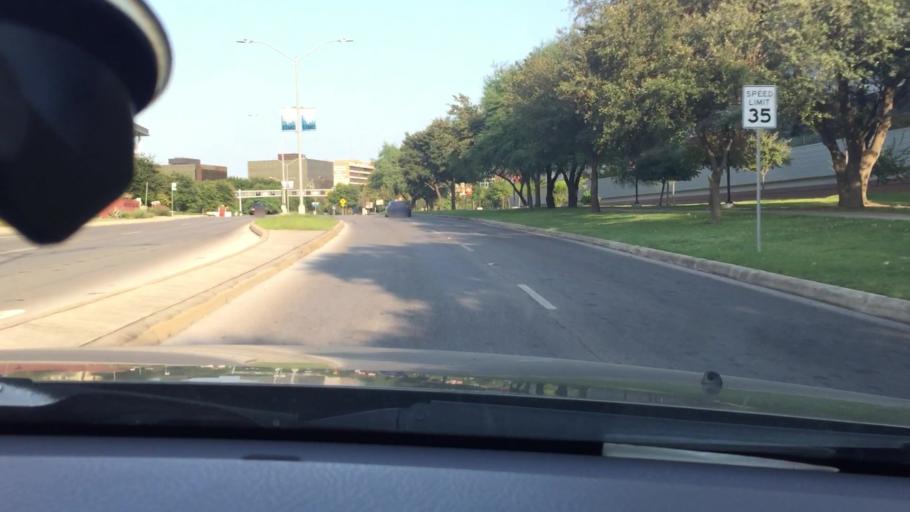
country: US
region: Texas
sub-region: Bexar County
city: Balcones Heights
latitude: 29.5147
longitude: -98.5824
